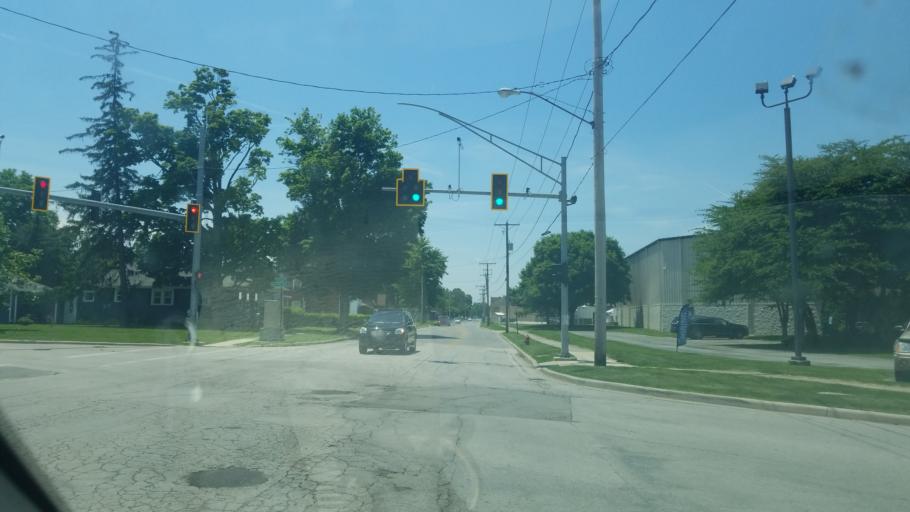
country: US
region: Ohio
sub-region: Hancock County
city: Findlay
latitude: 41.0537
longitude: -83.6414
